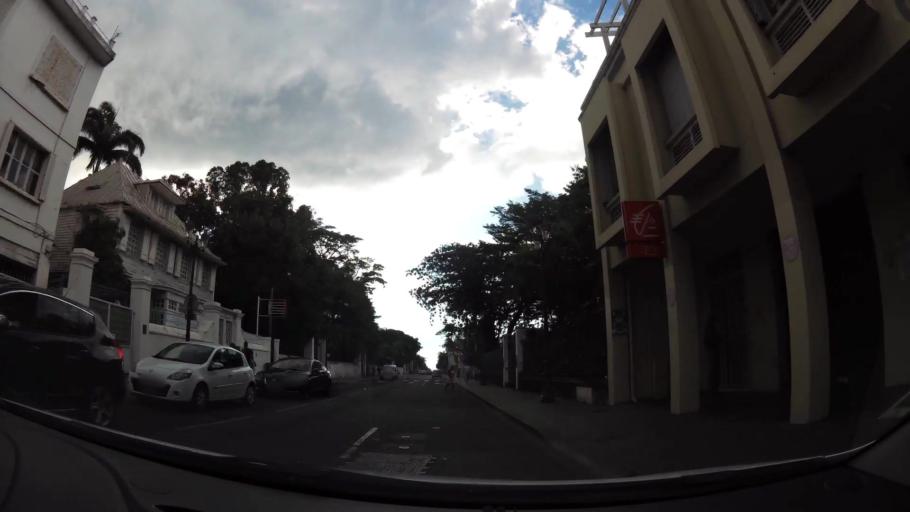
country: RE
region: Reunion
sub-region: Reunion
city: Saint-Denis
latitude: -20.8854
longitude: 55.4509
